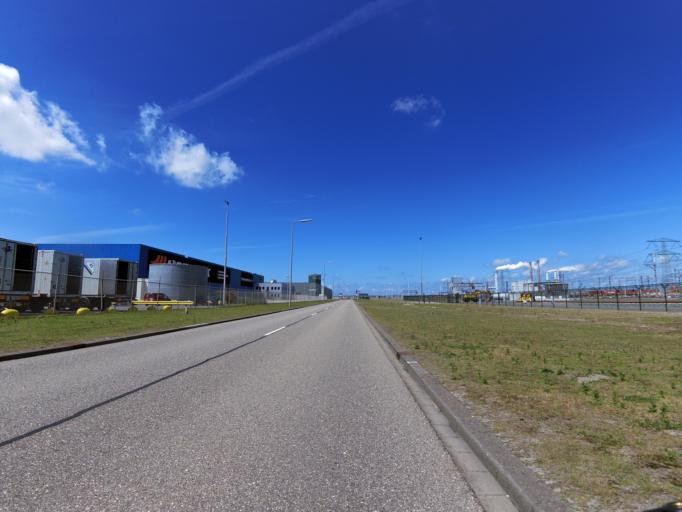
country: NL
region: South Holland
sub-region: Gemeente Rotterdam
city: Hoek van Holland
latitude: 51.9422
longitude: 4.0228
